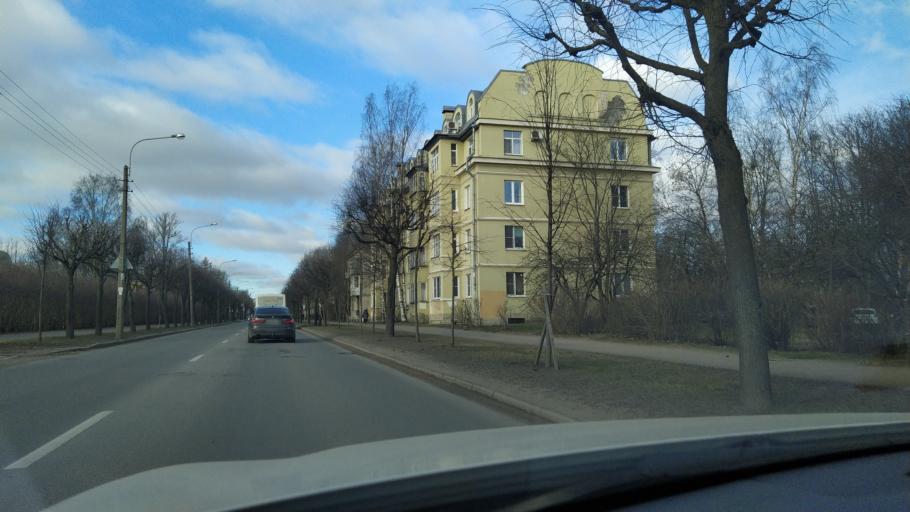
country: RU
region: St.-Petersburg
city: Pushkin
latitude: 59.7252
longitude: 30.4222
